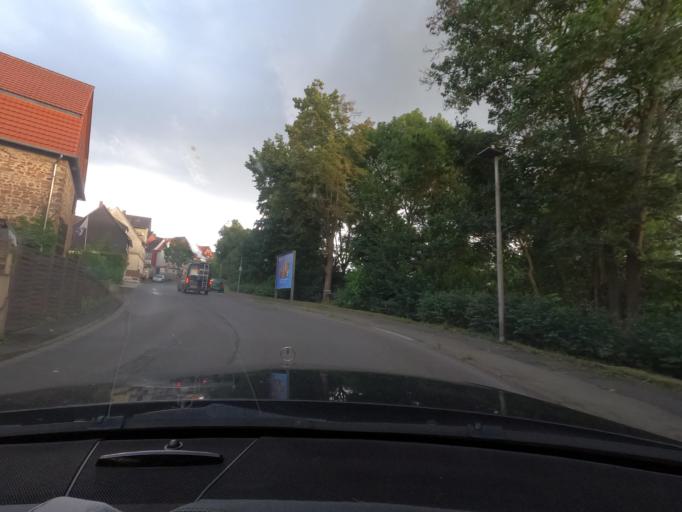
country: DE
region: Hesse
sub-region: Regierungsbezirk Kassel
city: Wolfhagen
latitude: 51.3261
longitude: 9.1659
